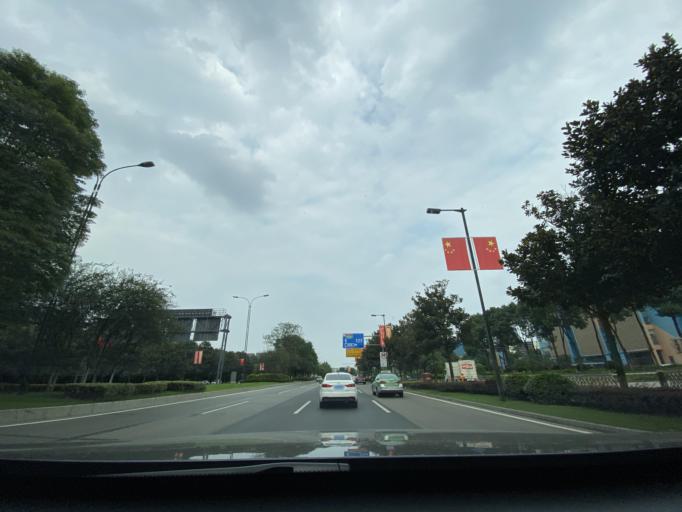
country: CN
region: Sichuan
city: Dongsheng
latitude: 30.6055
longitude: 103.9327
